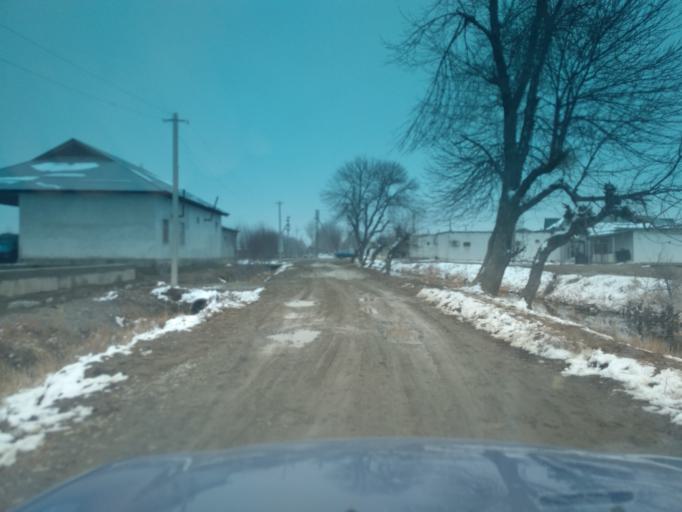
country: UZ
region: Sirdaryo
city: Guliston
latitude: 40.4786
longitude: 68.7497
